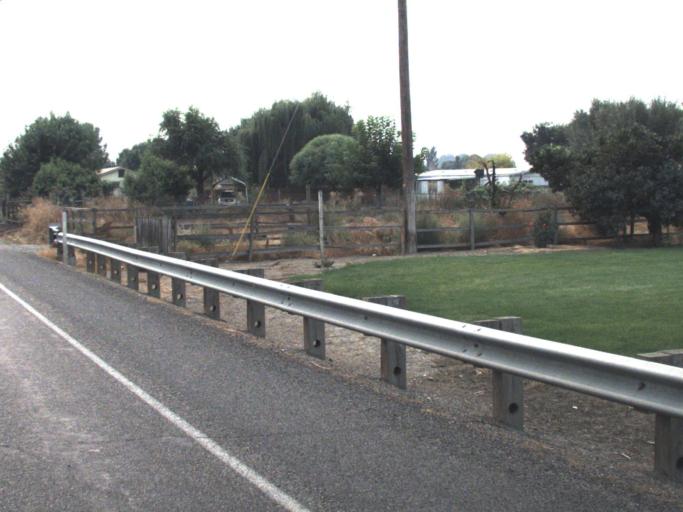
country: US
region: Washington
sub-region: Yakima County
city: Sunnyside
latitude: 46.2830
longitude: -119.9992
